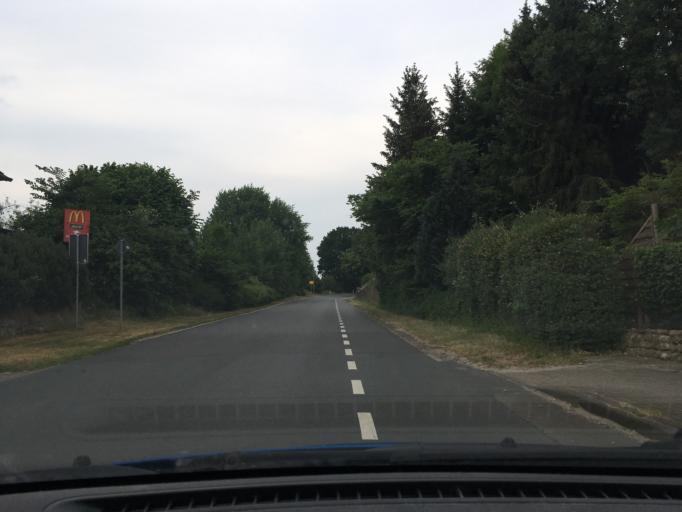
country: DE
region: Lower Saxony
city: Walsrode
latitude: 52.8327
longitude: 9.6316
